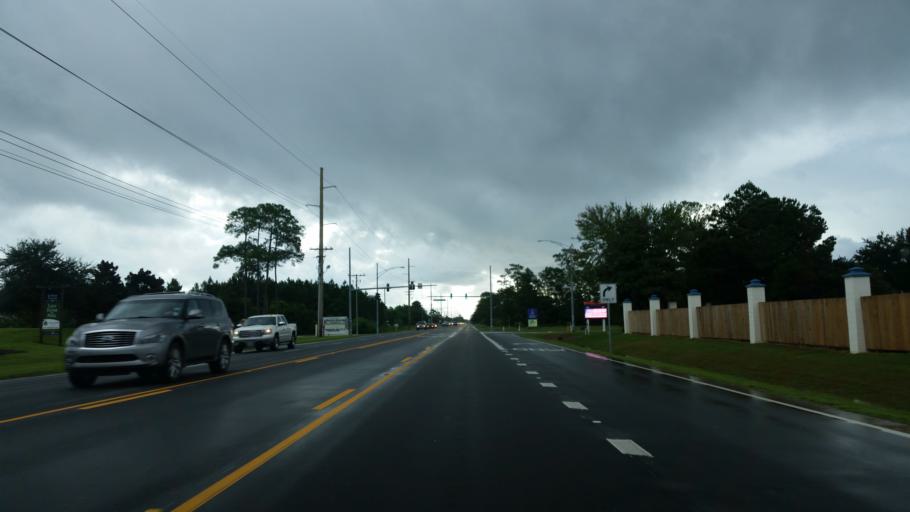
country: US
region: Alabama
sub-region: Baldwin County
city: Orange Beach
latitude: 30.2902
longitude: -87.6163
